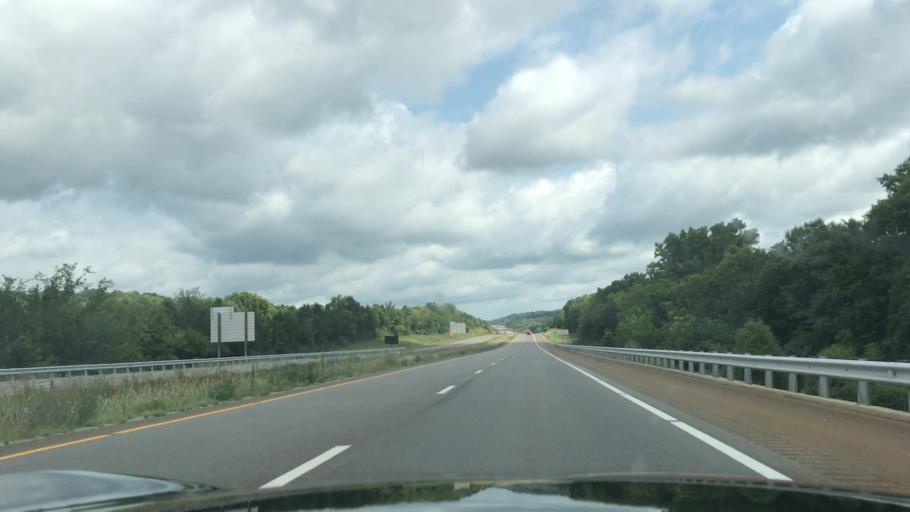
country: US
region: Kentucky
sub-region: Warren County
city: Bowling Green
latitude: 36.9776
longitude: -86.5008
